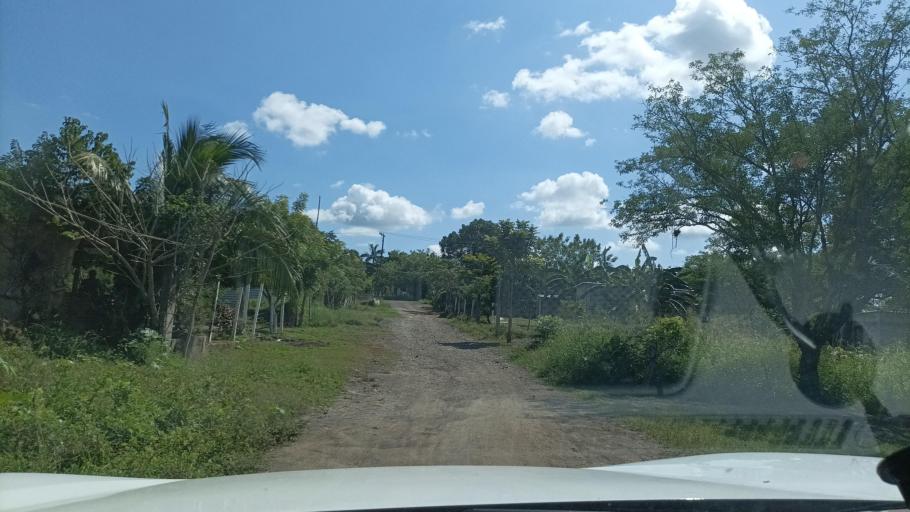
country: MX
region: Veracruz
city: Manlio Fabio Altamirano
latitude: 19.0900
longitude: -96.3400
